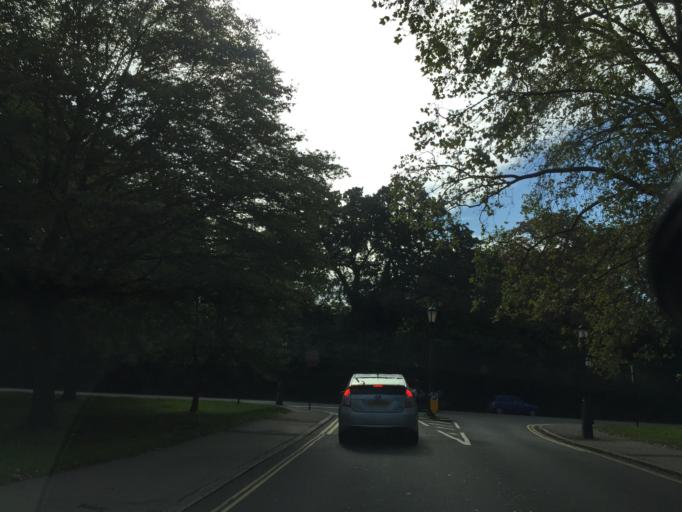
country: GB
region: England
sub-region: Greater London
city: Belsize Park
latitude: 51.5344
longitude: -0.1630
